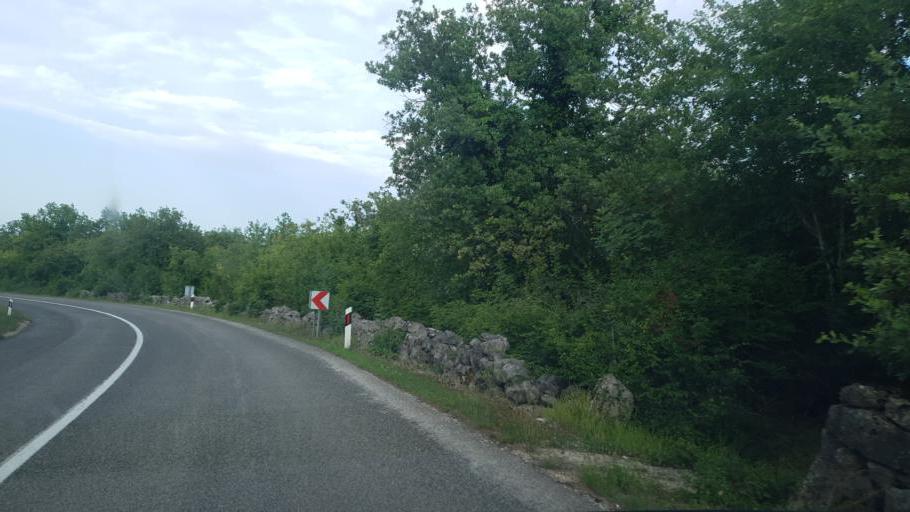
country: HR
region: Primorsko-Goranska
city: Njivice
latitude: 45.1263
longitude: 14.5727
